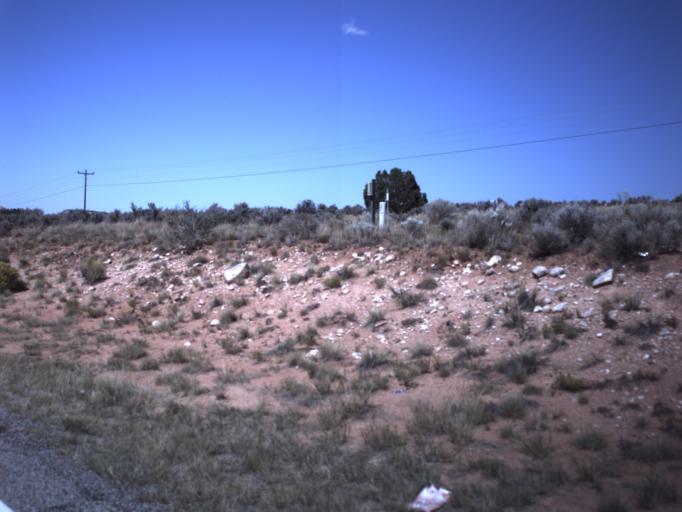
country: US
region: Utah
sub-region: Grand County
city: Moab
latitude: 38.3068
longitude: -109.3960
